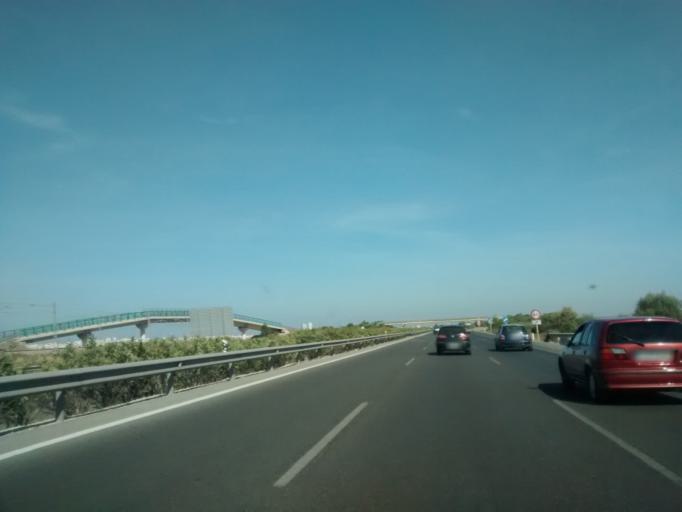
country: ES
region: Andalusia
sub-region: Provincia de Cadiz
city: Chiclana de la Frontera
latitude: 36.4504
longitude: -6.1507
